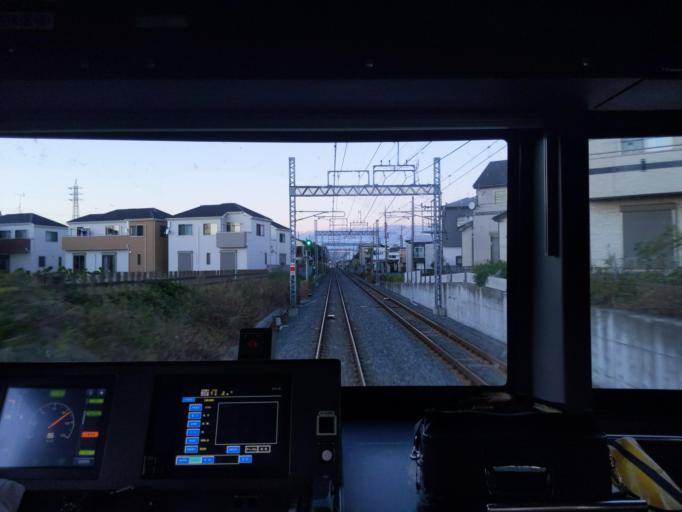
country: JP
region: Chiba
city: Kashiwa
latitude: 35.7983
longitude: 139.9991
